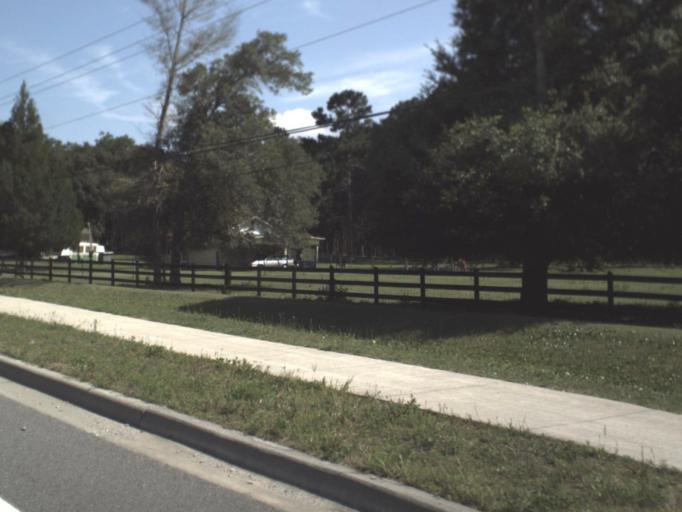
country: US
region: Florida
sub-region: Clay County
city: Green Cove Springs
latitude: 29.9660
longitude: -81.4977
